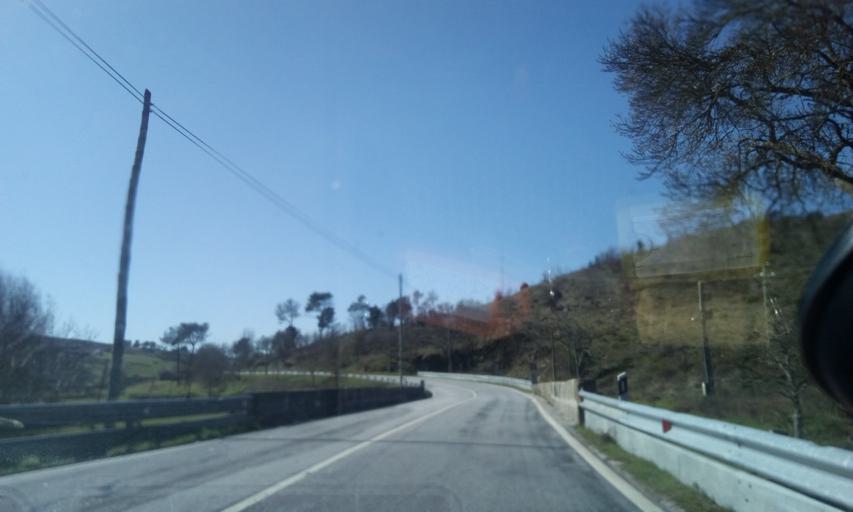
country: PT
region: Guarda
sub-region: Celorico da Beira
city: Celorico da Beira
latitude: 40.6007
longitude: -7.4255
